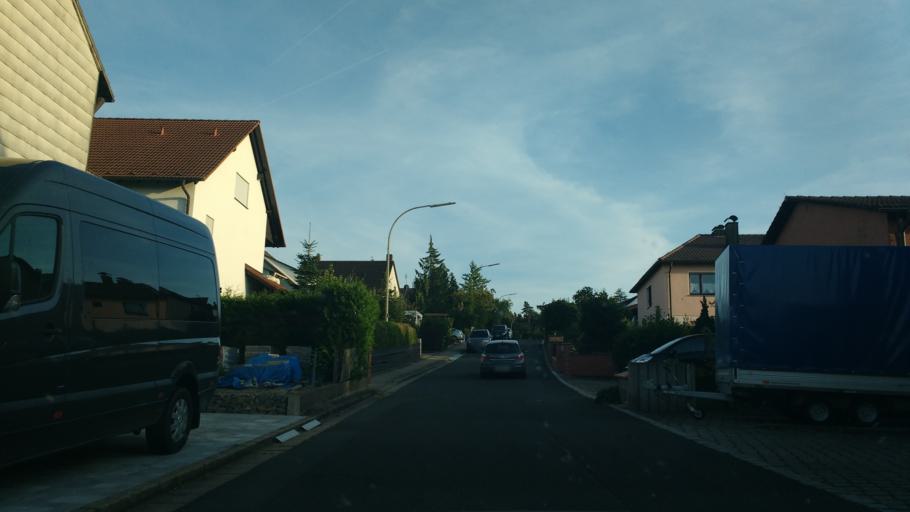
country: DE
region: Bavaria
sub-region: Regierungsbezirk Mittelfranken
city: Weisendorf
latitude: 49.6189
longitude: 10.8280
